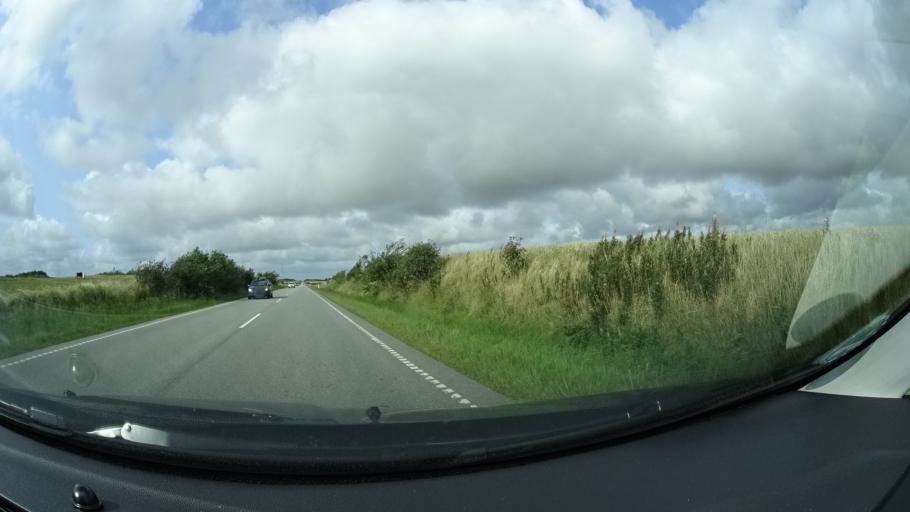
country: DK
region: Central Jutland
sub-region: Lemvig Kommune
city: Harboore
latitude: 56.5108
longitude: 8.1745
